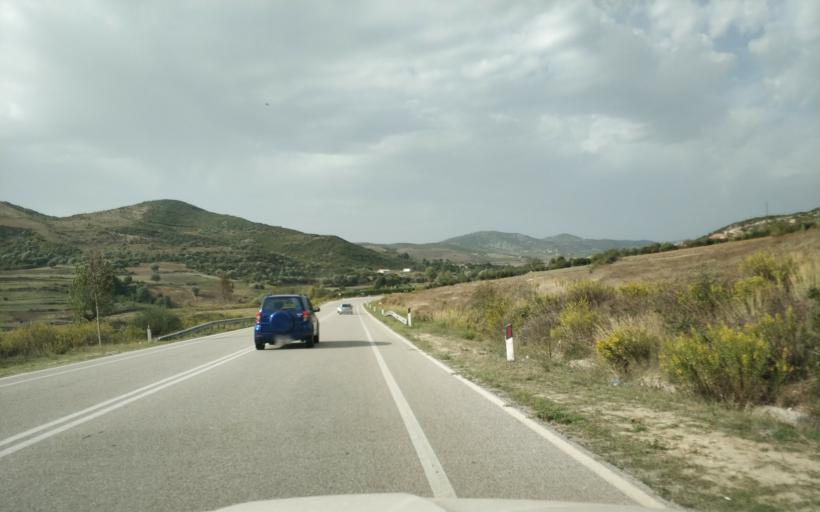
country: AL
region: Gjirokaster
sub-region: Rrethi i Tepelenes
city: Krahes
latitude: 40.4037
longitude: 19.8625
